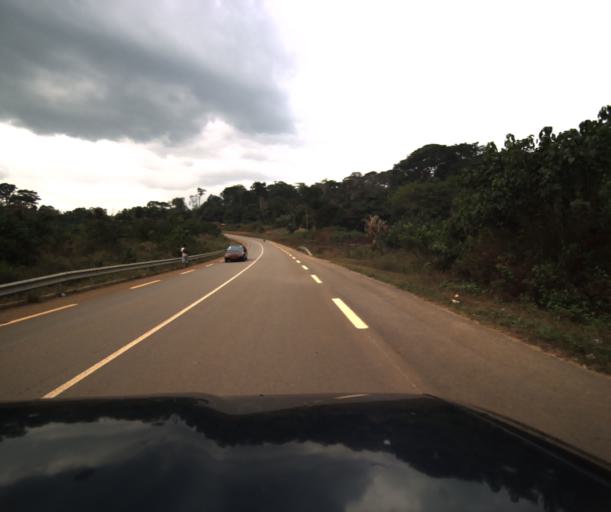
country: CM
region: Centre
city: Akono
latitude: 3.6095
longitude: 11.3149
